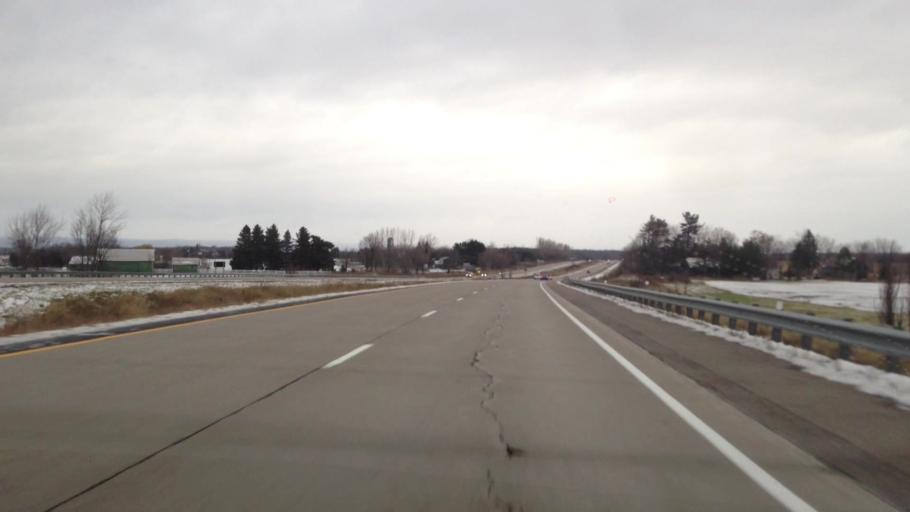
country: CA
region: Ontario
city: Hawkesbury
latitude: 45.5294
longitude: -74.5562
